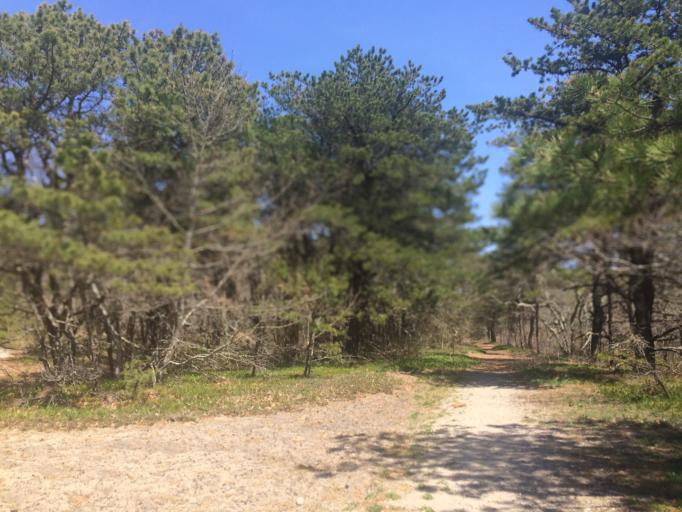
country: US
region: Massachusetts
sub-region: Barnstable County
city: Provincetown
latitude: 42.0625
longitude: -70.1759
